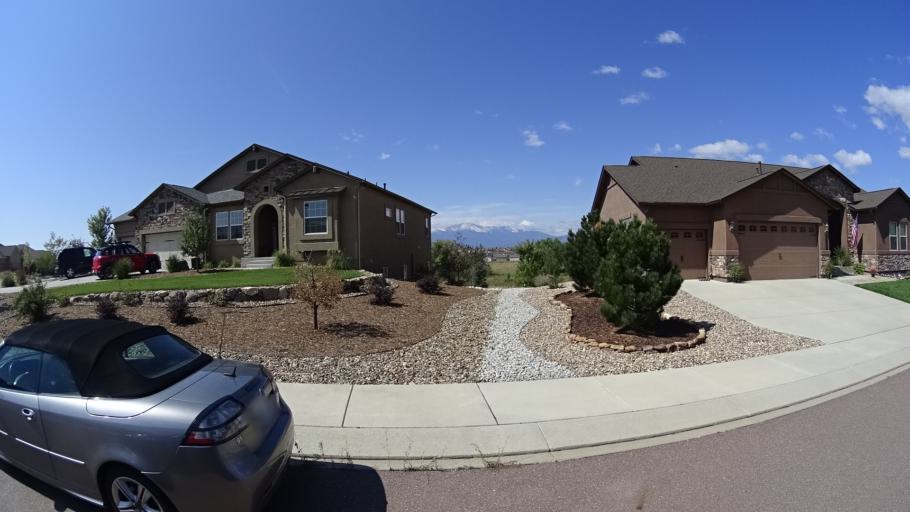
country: US
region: Colorado
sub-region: El Paso County
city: Cimarron Hills
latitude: 38.9322
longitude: -104.6867
